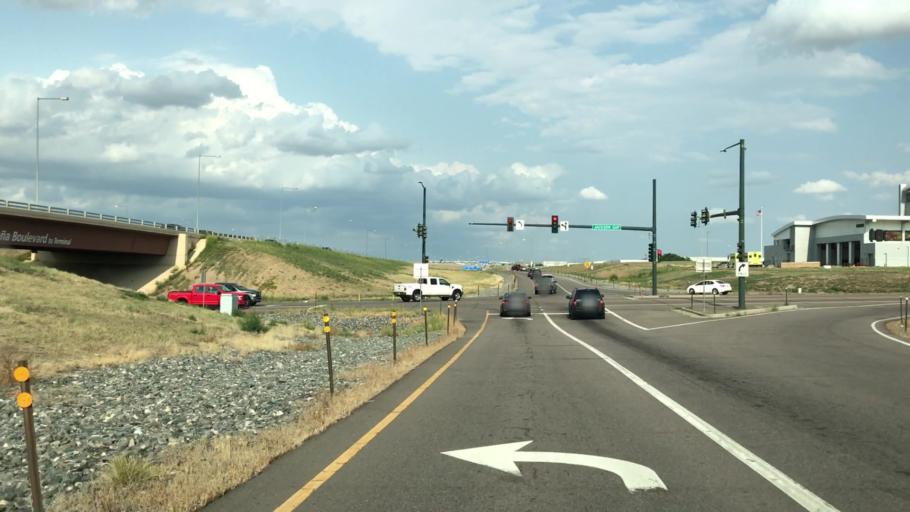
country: US
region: Colorado
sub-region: Adams County
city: Aurora
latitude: 39.8331
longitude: -104.6938
